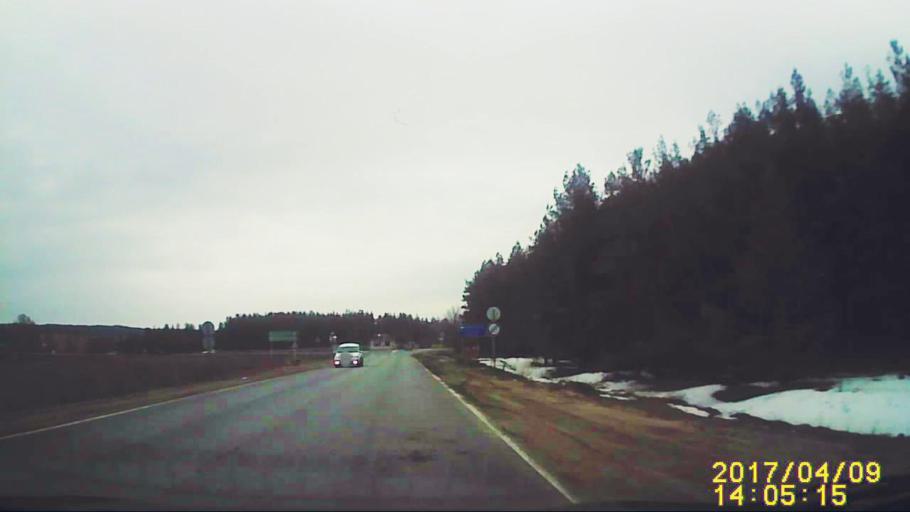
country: RU
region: Ulyanovsk
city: Silikatnyy
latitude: 53.9992
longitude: 48.2189
